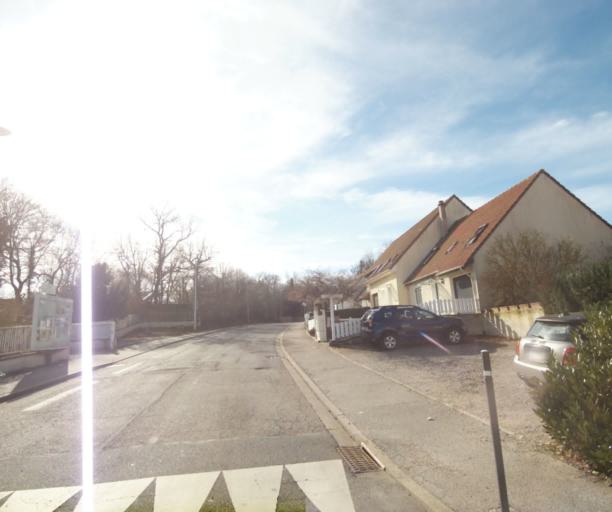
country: FR
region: Lorraine
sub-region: Departement de Meurthe-et-Moselle
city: Villers-les-Nancy
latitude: 48.6523
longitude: 6.1606
